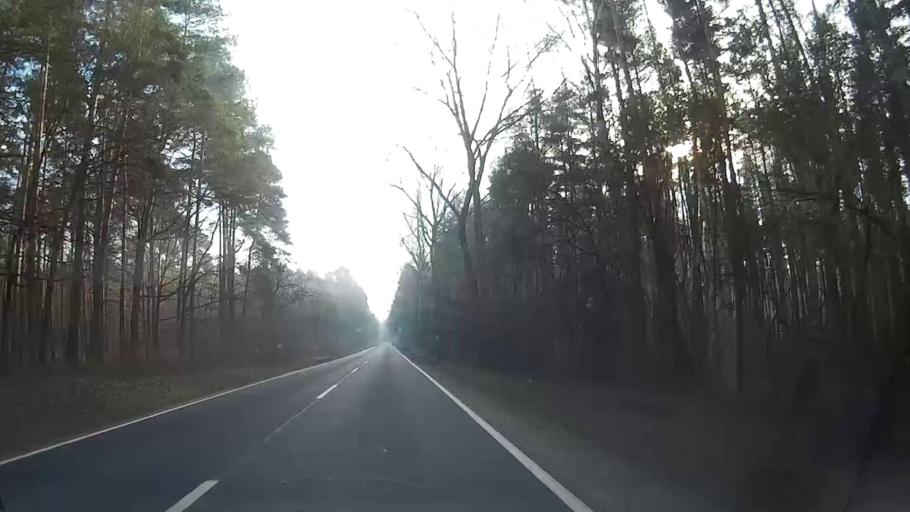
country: PL
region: Lesser Poland Voivodeship
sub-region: Powiat chrzanowski
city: Zagorze
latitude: 50.0732
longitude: 19.3933
